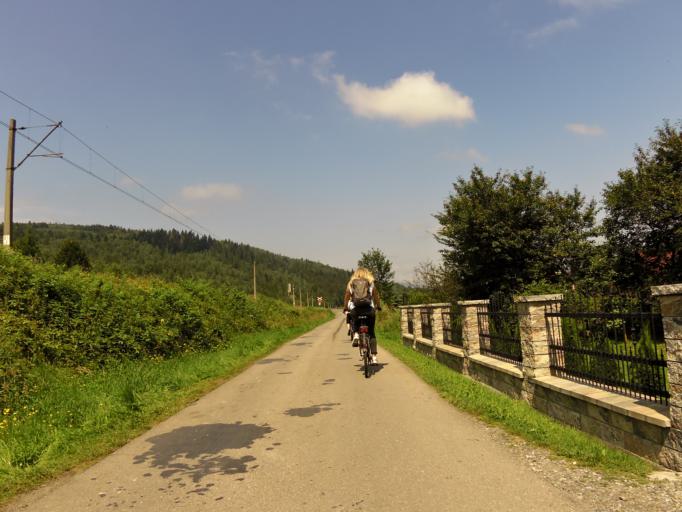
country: PL
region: Silesian Voivodeship
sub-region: Powiat zywiecki
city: Rajcza
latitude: 49.5212
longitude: 19.1093
